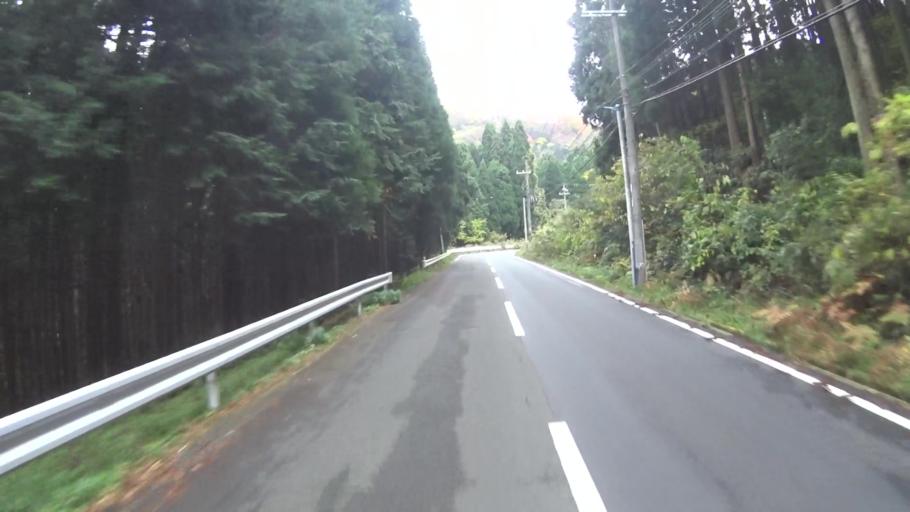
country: JP
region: Kyoto
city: Maizuru
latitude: 35.5536
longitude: 135.4553
